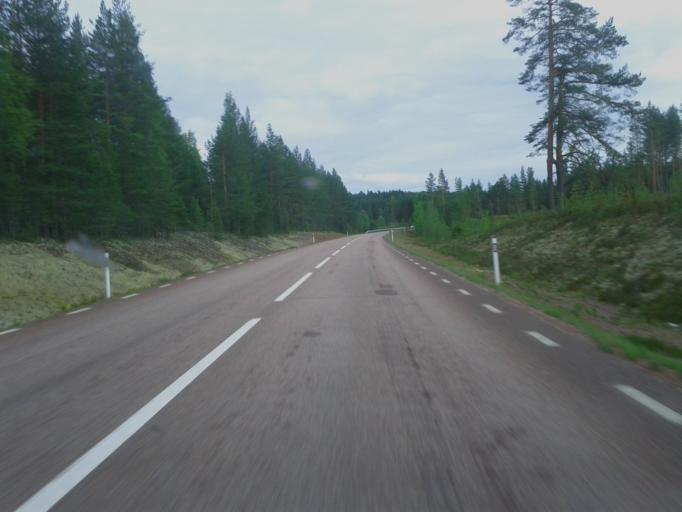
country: SE
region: Dalarna
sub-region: Mora Kommun
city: Mora
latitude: 61.1053
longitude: 14.2866
